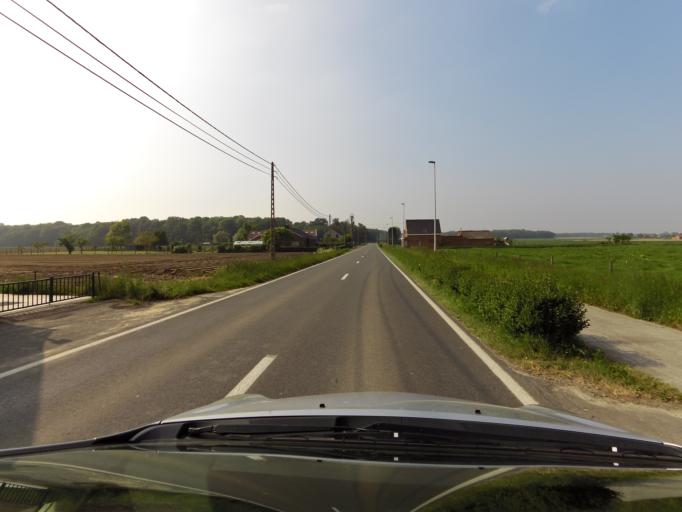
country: BE
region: Flanders
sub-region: Provincie West-Vlaanderen
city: Poperinge
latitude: 50.8761
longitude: 2.7057
